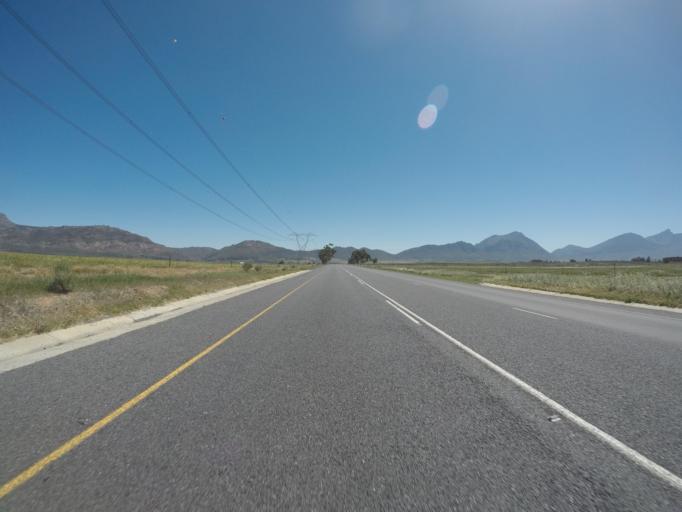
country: ZA
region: Western Cape
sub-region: Cape Winelands District Municipality
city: Ceres
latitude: -33.3210
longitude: 19.1405
